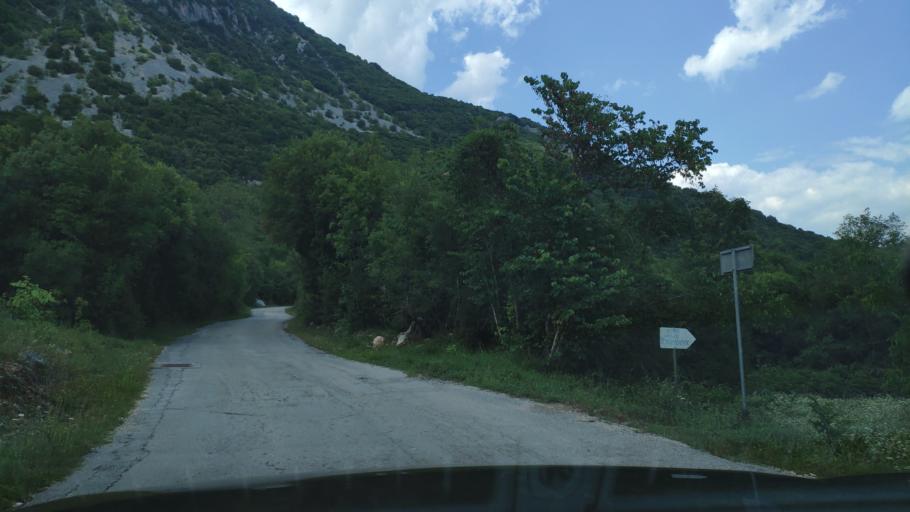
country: GR
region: Epirus
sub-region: Nomos Artas
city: Agios Dimitrios
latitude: 39.4457
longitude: 21.0171
